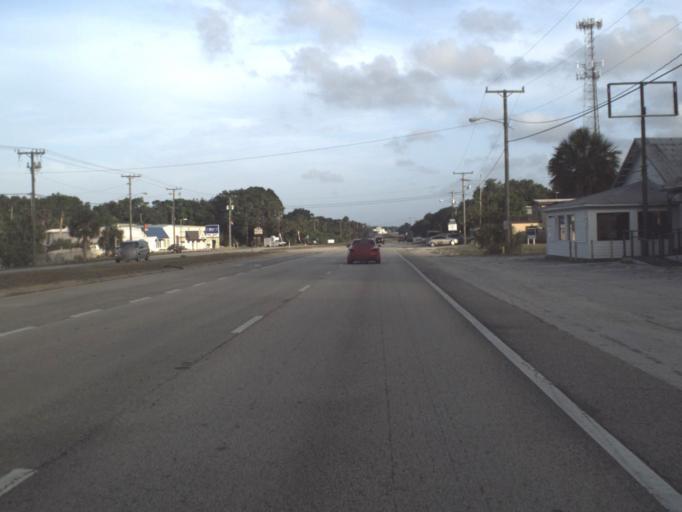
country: US
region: Florida
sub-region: Brevard County
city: Rockledge
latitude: 28.3132
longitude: -80.7100
